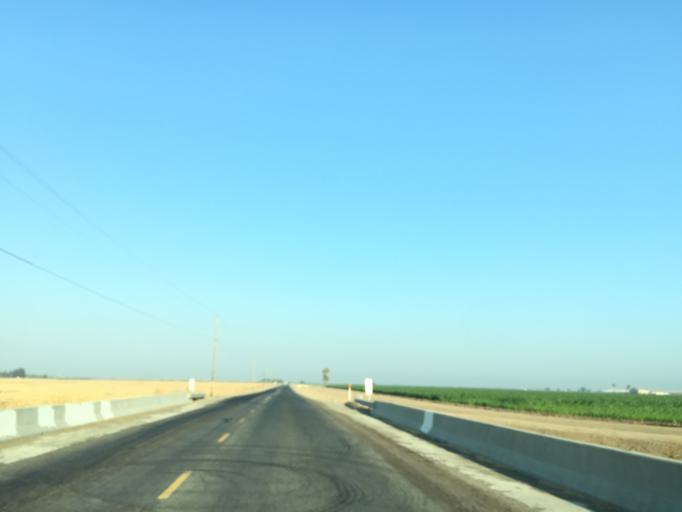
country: US
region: California
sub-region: Tulare County
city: Cutler
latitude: 36.4580
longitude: -119.3346
